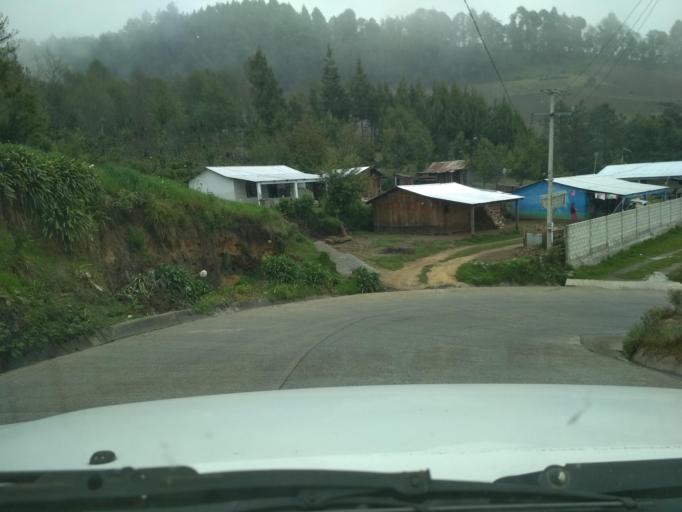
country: MX
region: Veracruz
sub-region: La Perla
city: Chilapa
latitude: 18.9763
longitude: -97.2016
